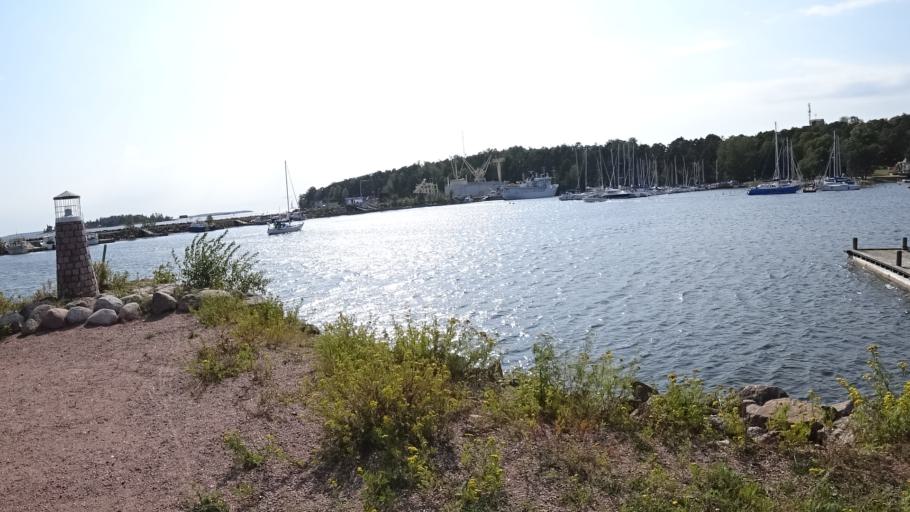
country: FI
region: Kymenlaakso
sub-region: Kotka-Hamina
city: Kotka
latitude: 60.4577
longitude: 26.9556
